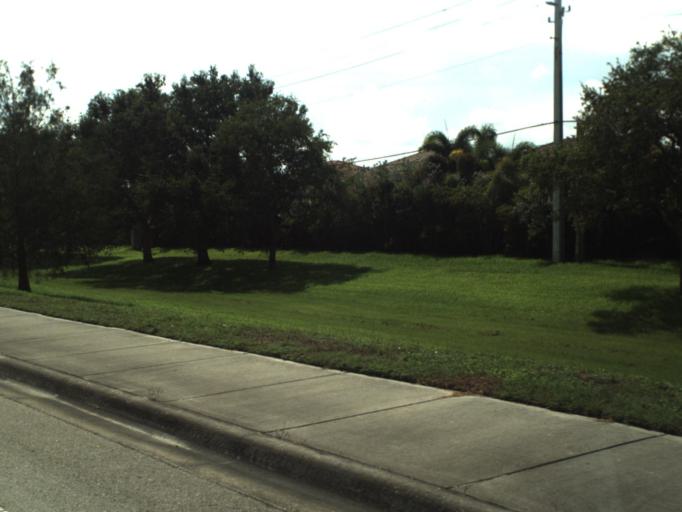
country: US
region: Florida
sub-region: Broward County
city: Sunshine Ranches
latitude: 26.0635
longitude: -80.3081
